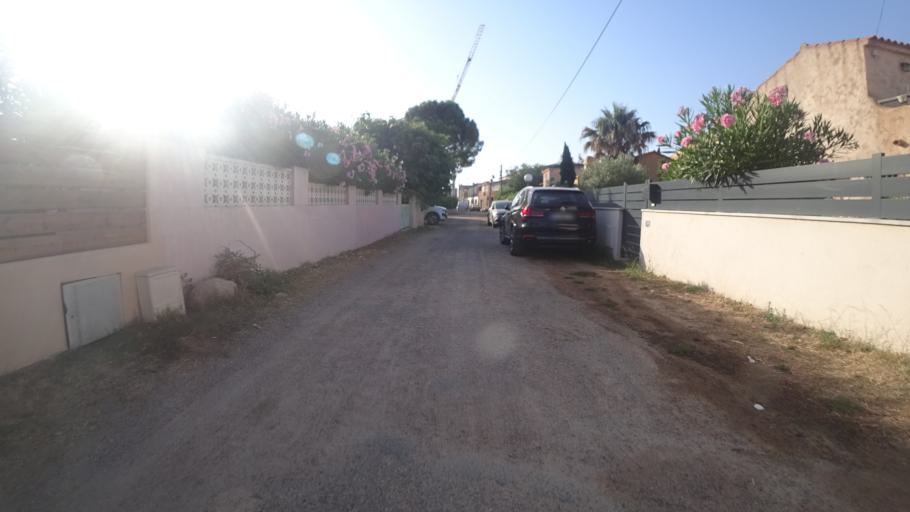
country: FR
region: Corsica
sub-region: Departement de la Corse-du-Sud
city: Porto-Vecchio
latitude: 41.6391
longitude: 9.3458
